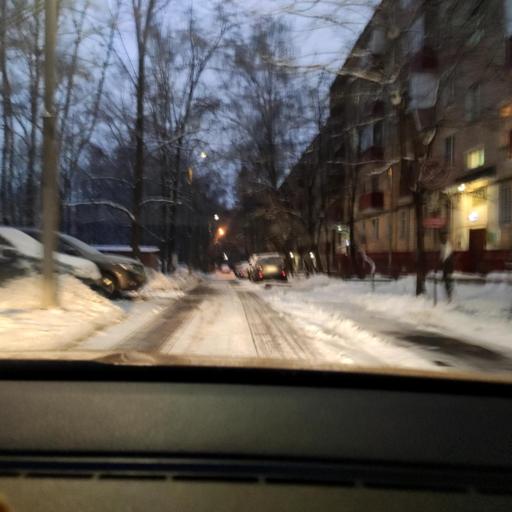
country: RU
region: Moskovskaya
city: Bol'shaya Setun'
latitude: 55.7388
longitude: 37.3975
